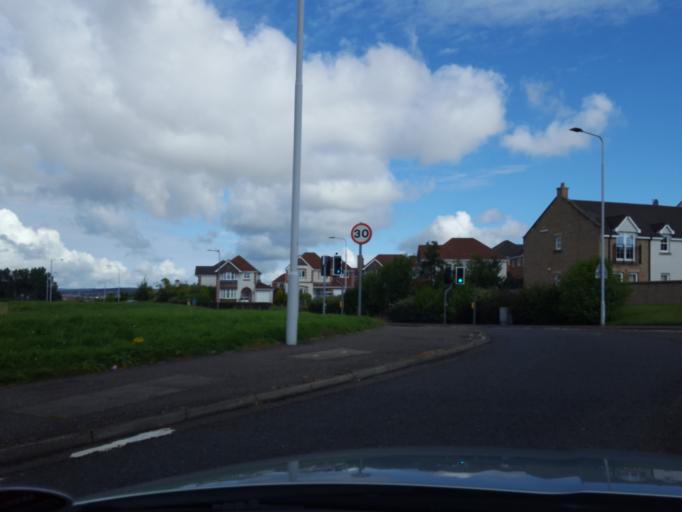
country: GB
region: Scotland
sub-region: Fife
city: Inverkeithing
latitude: 56.0515
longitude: -3.4120
